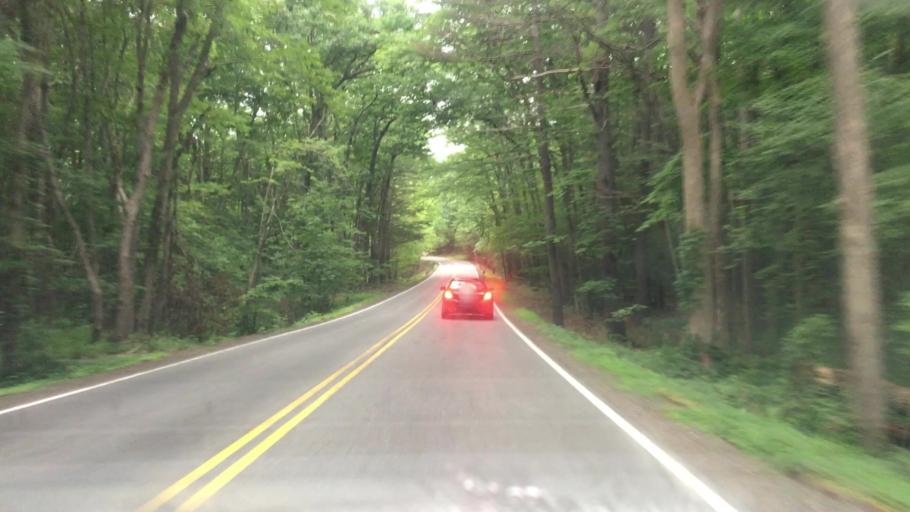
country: US
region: New Hampshire
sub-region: Rockingham County
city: Greenland
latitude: 43.0878
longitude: -70.8365
